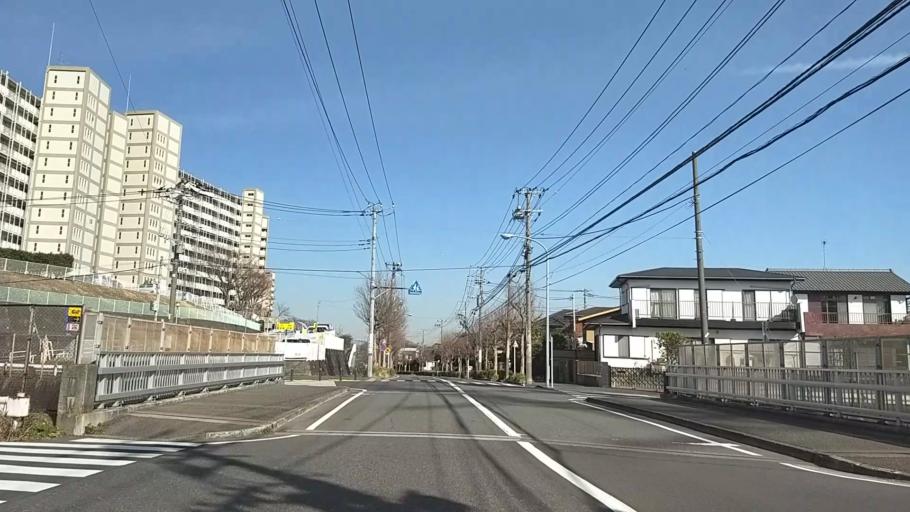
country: JP
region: Kanagawa
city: Kamakura
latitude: 35.3755
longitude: 139.5858
